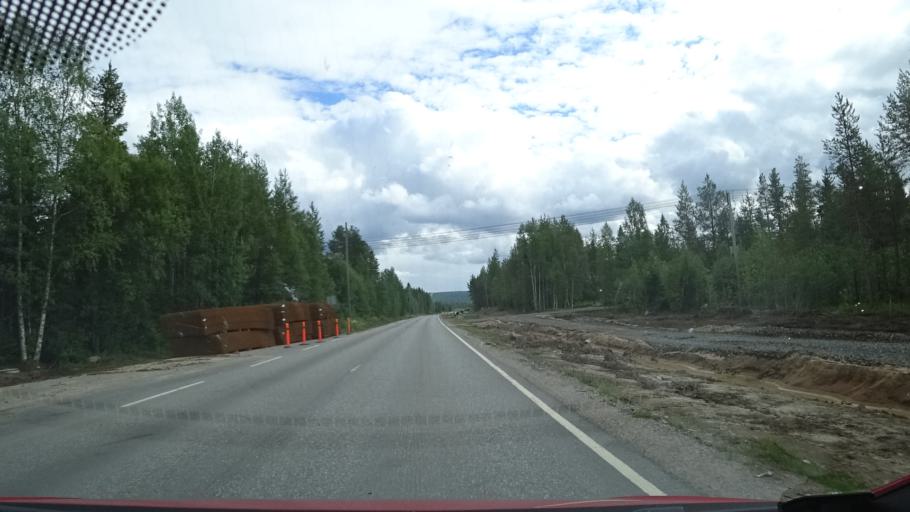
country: FI
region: Lapland
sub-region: Rovaniemi
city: Rovaniemi
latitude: 66.5341
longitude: 25.7314
